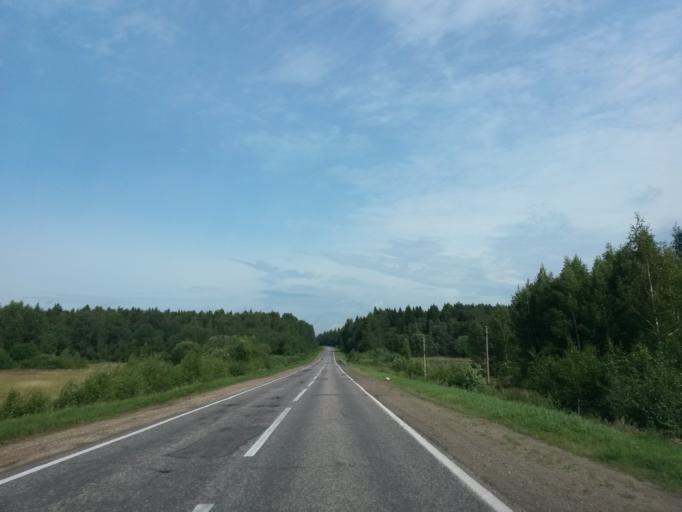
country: RU
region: Jaroslavl
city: Krasnyye Tkachi
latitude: 57.4648
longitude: 39.9087
